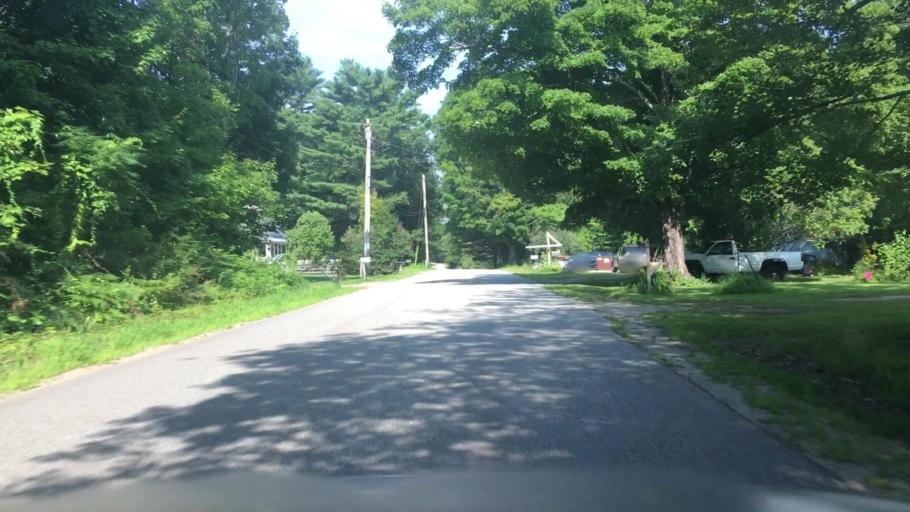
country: US
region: Maine
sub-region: Kennebec County
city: Monmouth
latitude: 44.2421
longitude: -70.0859
